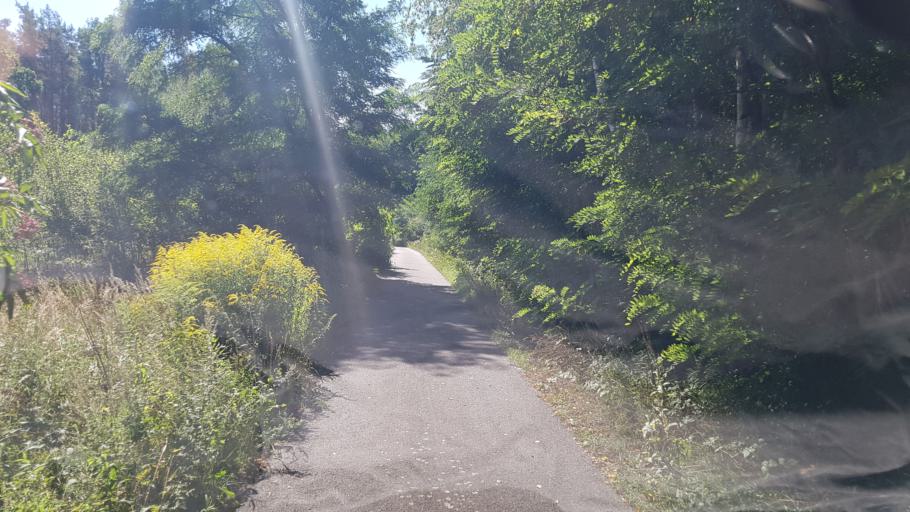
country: DE
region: Brandenburg
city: Altdobern
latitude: 51.6975
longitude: 14.0001
